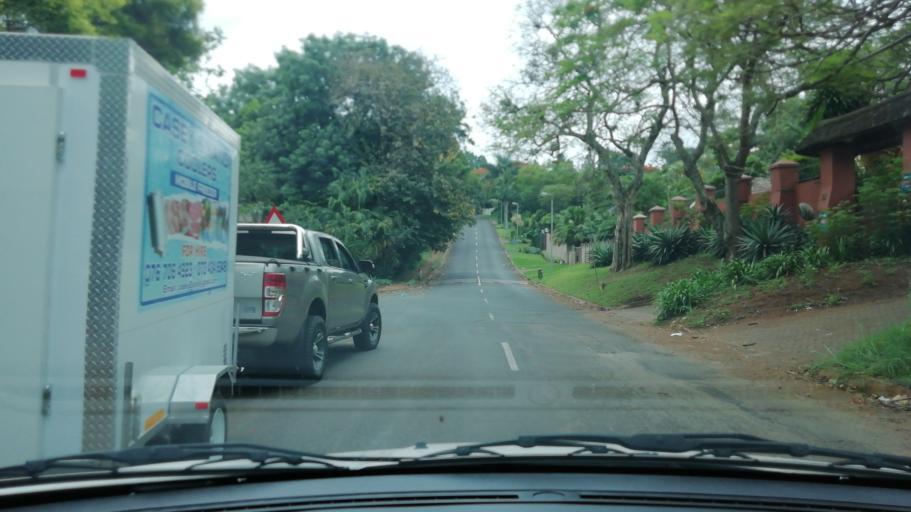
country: ZA
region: KwaZulu-Natal
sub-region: uThungulu District Municipality
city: Empangeni
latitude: -28.7526
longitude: 31.8923
